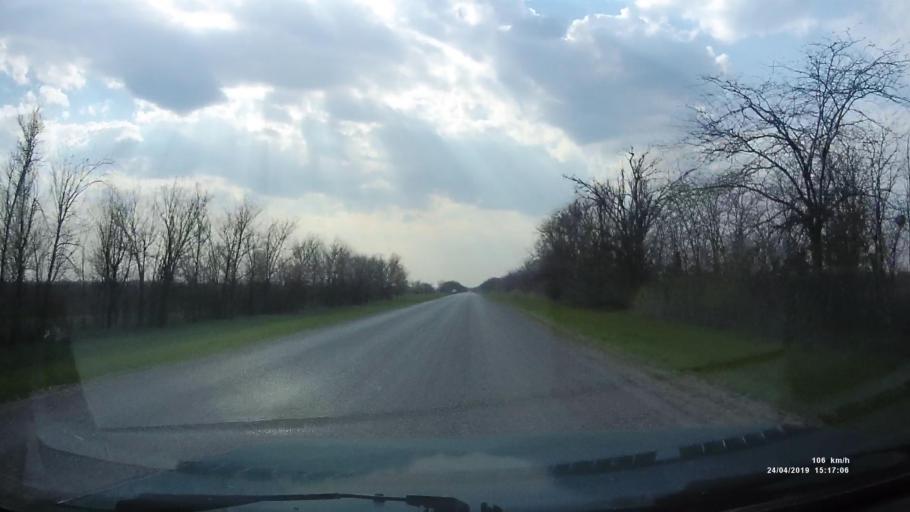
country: RU
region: Rostov
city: Remontnoye
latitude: 46.5465
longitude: 43.1974
